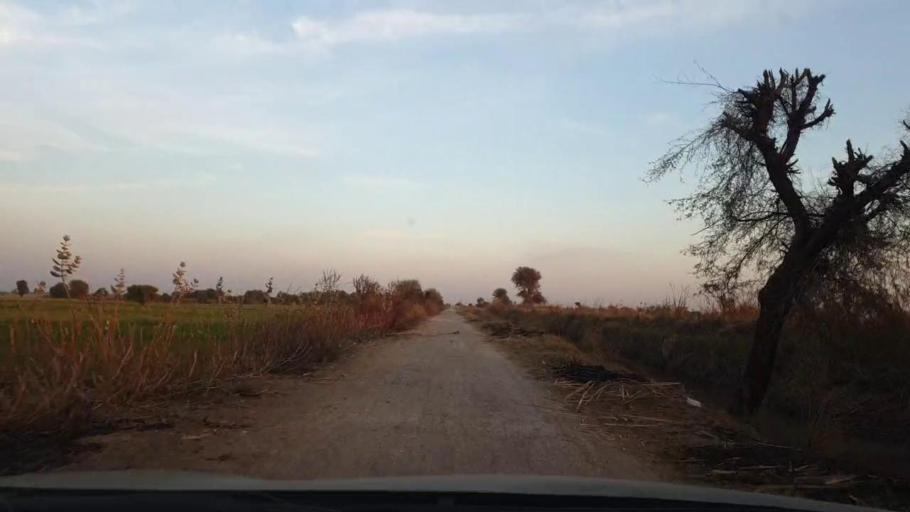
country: PK
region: Sindh
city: Tando Allahyar
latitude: 25.5867
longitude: 68.7179
